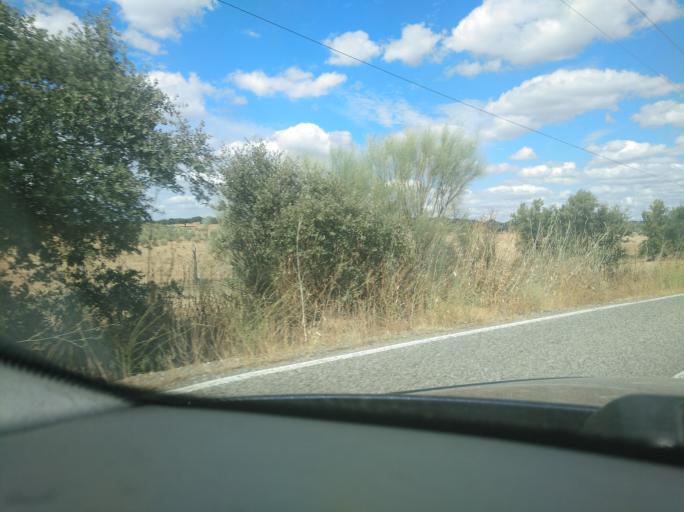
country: PT
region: Portalegre
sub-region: Arronches
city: Arronches
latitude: 39.0823
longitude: -7.3615
